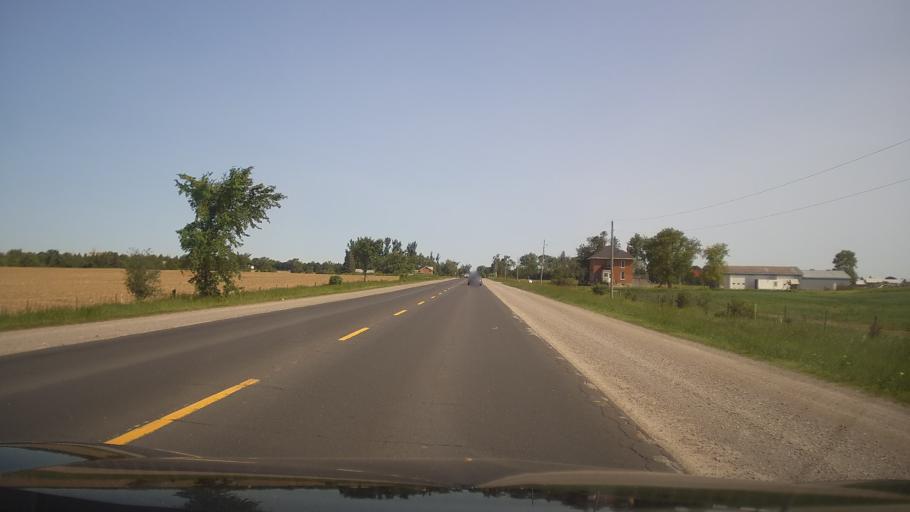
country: CA
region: Ontario
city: Omemee
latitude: 44.3272
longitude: -78.6859
